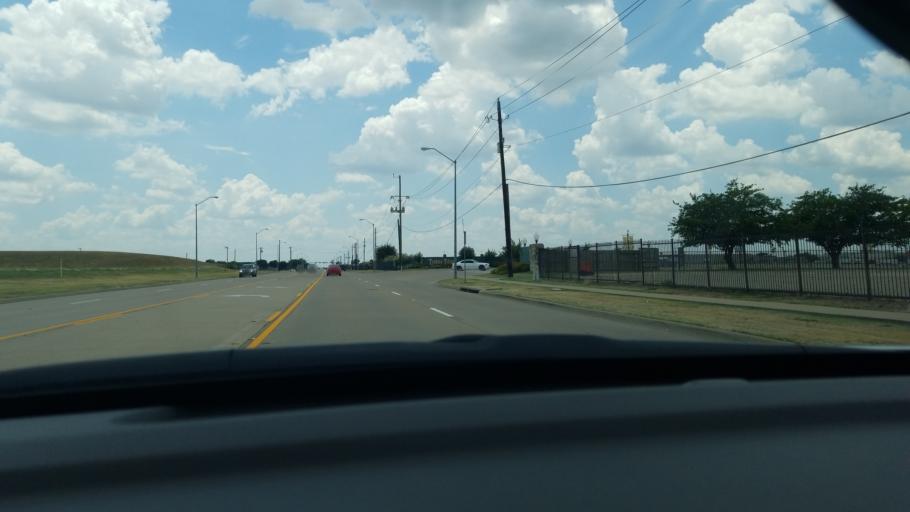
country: US
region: Texas
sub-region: Tarrant County
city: Arlington
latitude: 32.6915
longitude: -97.0493
